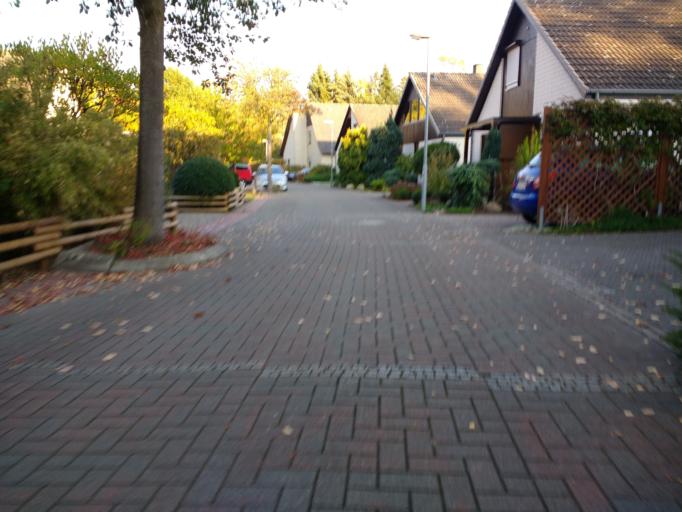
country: DE
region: Lower Saxony
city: Gifhorn
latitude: 52.4661
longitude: 10.5663
